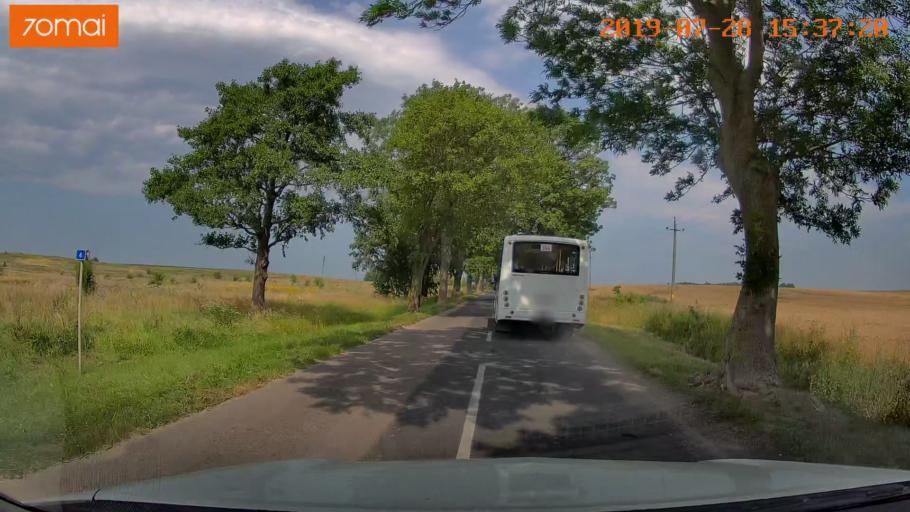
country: RU
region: Kaliningrad
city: Donskoye
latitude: 54.8910
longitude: 19.9981
